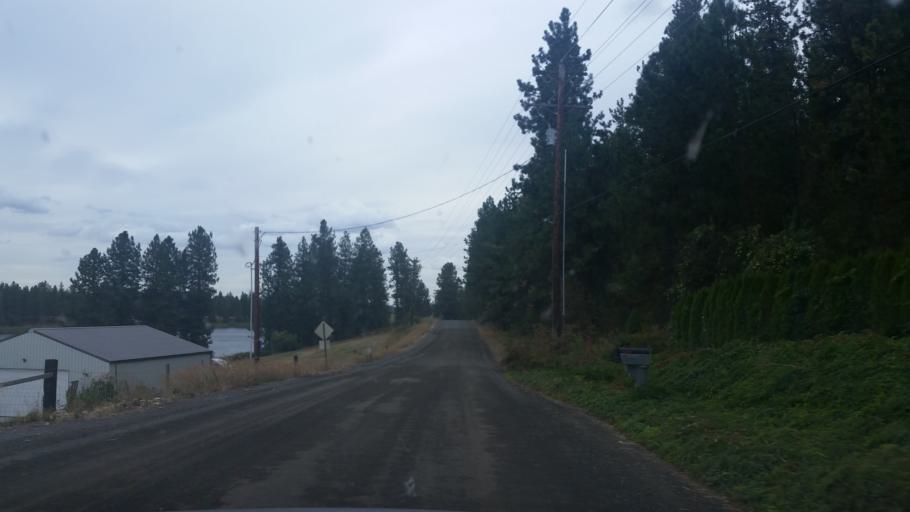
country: US
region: Washington
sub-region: Spokane County
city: Cheney
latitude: 47.5495
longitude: -117.5988
